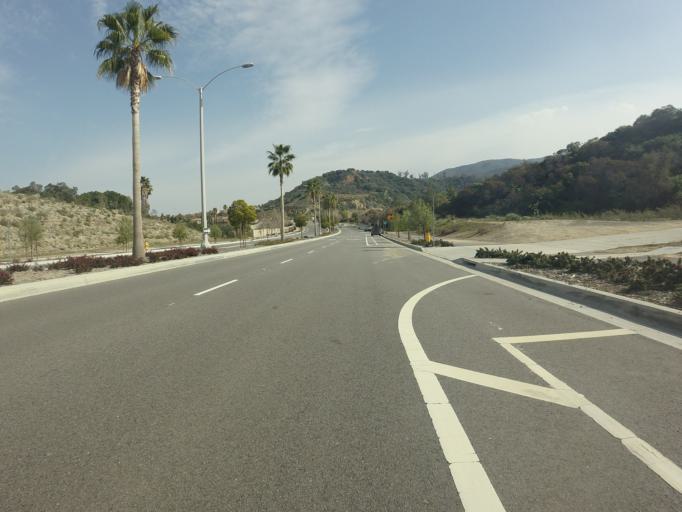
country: US
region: California
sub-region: Riverside County
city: Corona
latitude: 33.8437
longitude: -117.6010
